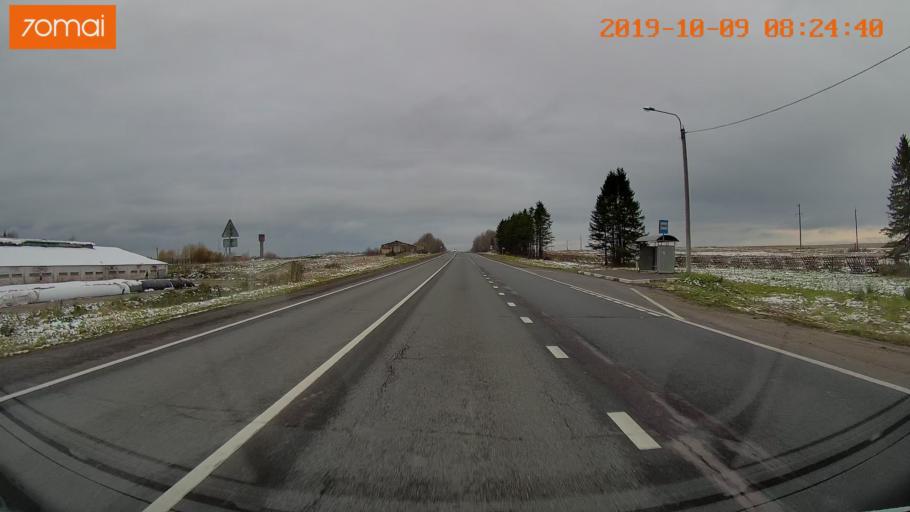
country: RU
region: Vologda
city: Gryazovets
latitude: 58.7696
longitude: 40.2770
